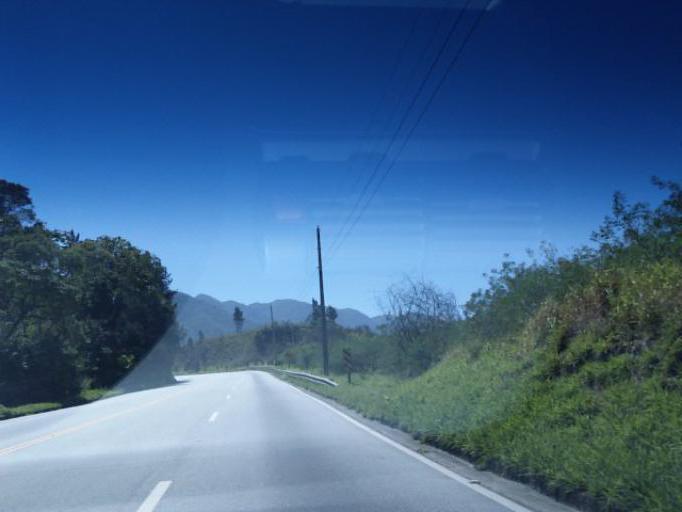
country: BR
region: Sao Paulo
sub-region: Campos Do Jordao
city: Campos do Jordao
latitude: -22.8387
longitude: -45.6207
